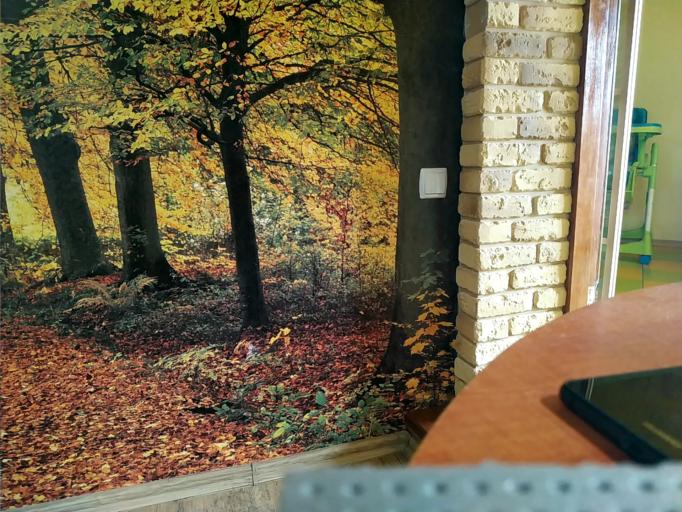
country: RU
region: Tverskaya
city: Kalashnikovo
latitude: 57.2972
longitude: 35.0994
